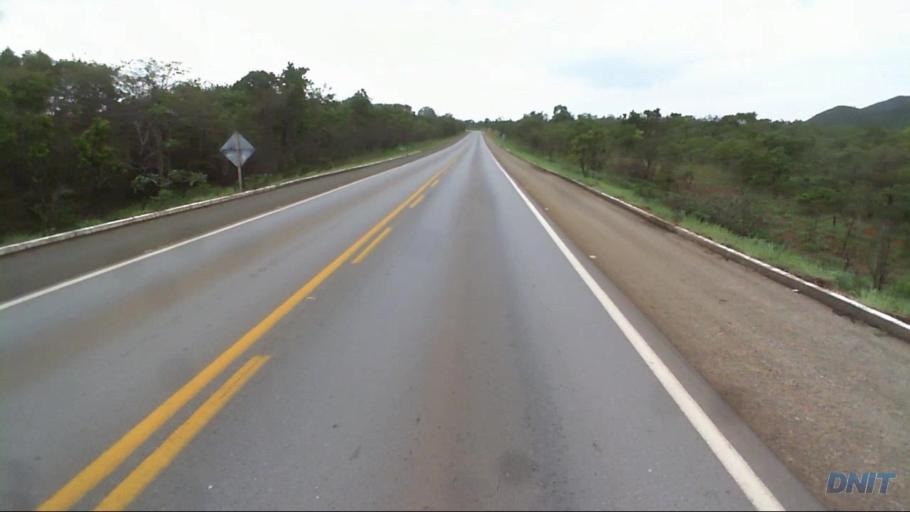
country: BR
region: Goias
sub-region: Barro Alto
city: Barro Alto
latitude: -14.7700
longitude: -49.0578
